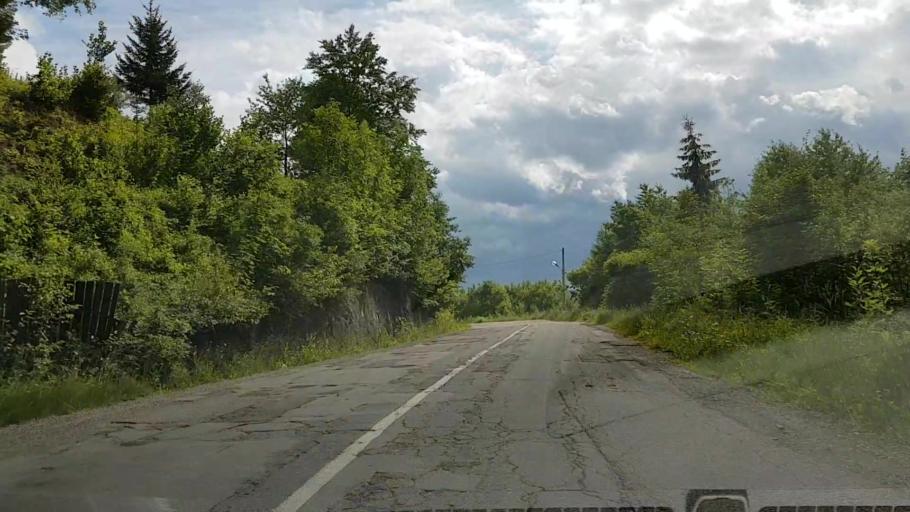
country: RO
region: Neamt
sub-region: Comuna Bicaz
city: Dodeni
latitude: 46.9942
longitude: 26.1015
